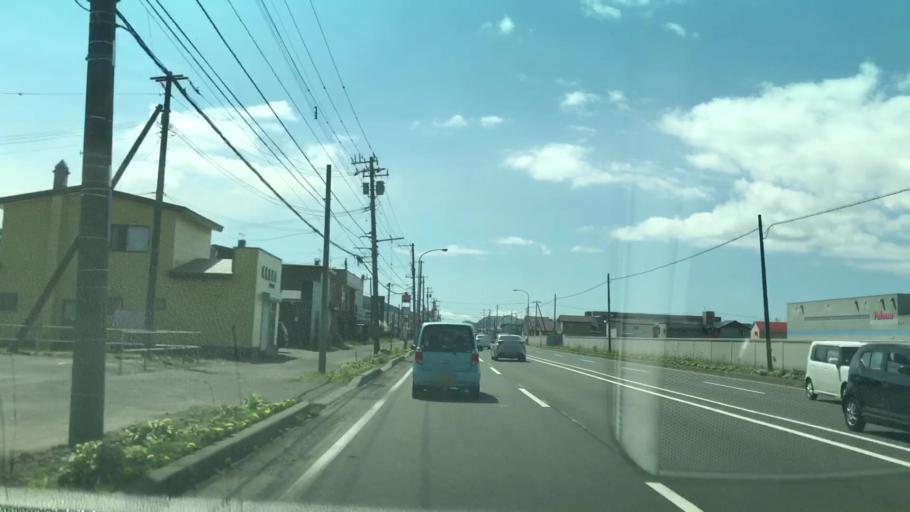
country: JP
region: Hokkaido
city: Muroran
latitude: 42.3703
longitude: 141.0633
